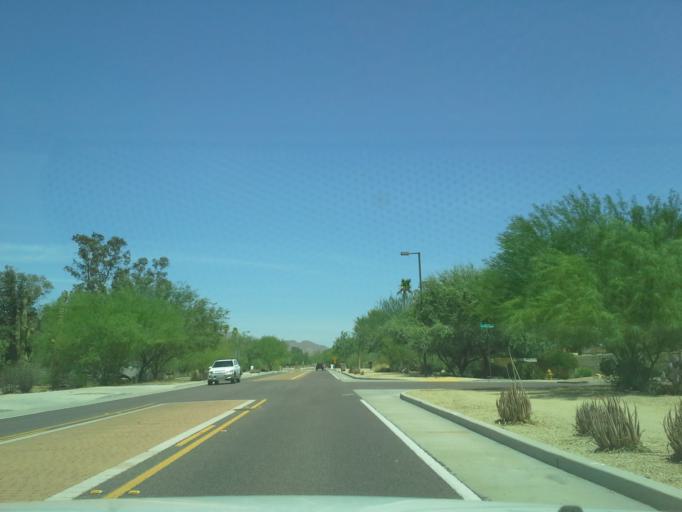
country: US
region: Arizona
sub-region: Maricopa County
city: Scottsdale
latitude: 33.5970
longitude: -111.8686
